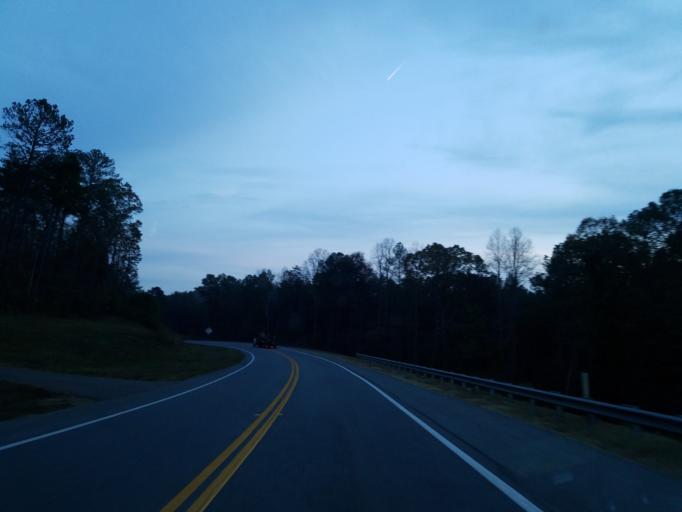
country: US
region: Georgia
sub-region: Pickens County
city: Jasper
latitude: 34.5254
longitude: -84.5714
